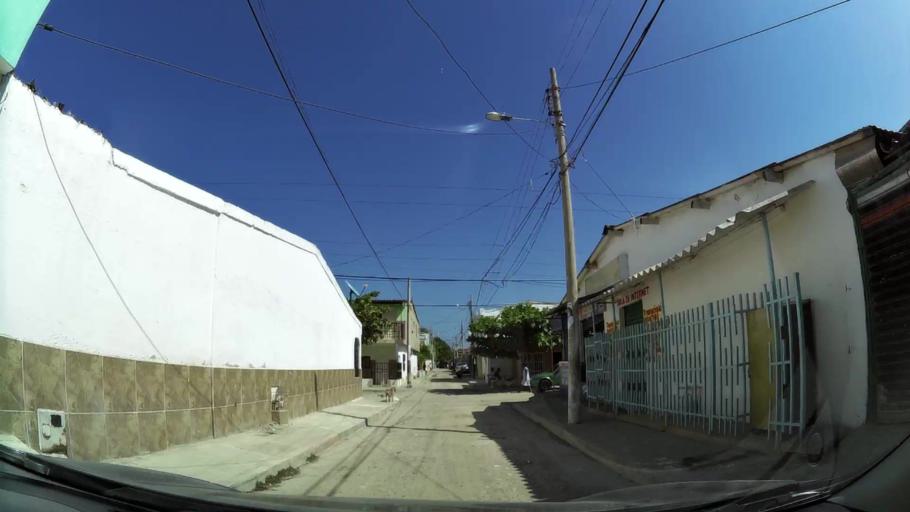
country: CO
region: Bolivar
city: Cartagena
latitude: 10.4391
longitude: -75.5151
